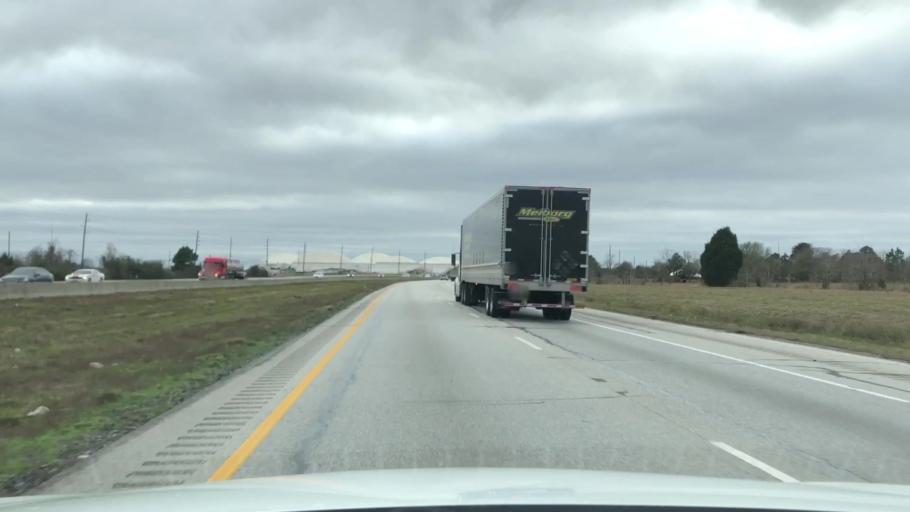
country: US
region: Texas
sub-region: Austin County
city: Sealy
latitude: 29.7703
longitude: -96.1385
